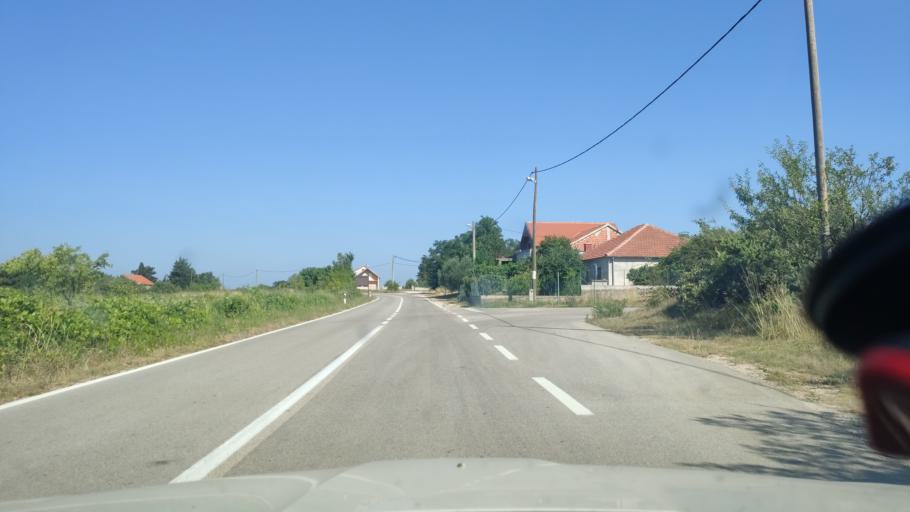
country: HR
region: Sibensko-Kniniska
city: Zaton
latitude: 43.9113
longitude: 15.8470
